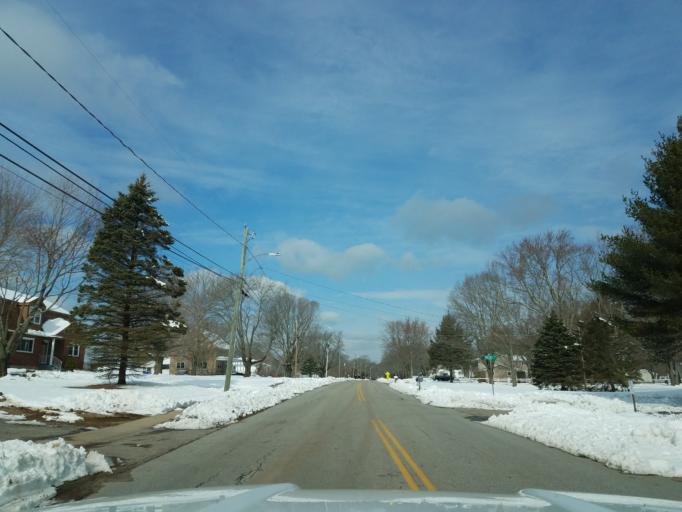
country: US
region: Connecticut
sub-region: New London County
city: Colchester
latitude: 41.5817
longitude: -72.3425
